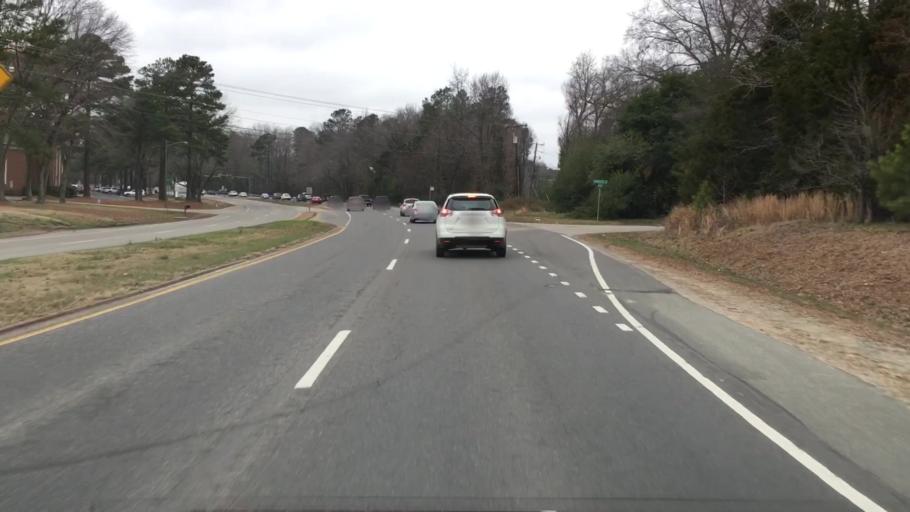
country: US
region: Virginia
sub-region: Chesterfield County
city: Bon Air
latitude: 37.5334
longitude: -77.5887
